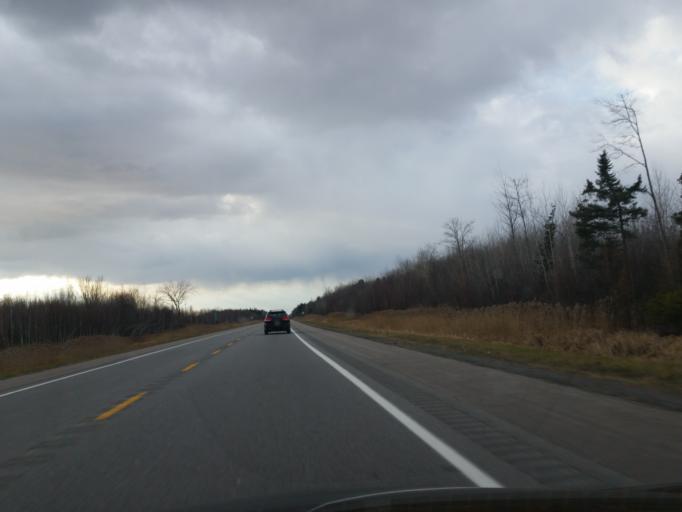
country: CA
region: Quebec
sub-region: Laurentides
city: Lachute
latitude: 45.6427
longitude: -74.2688
